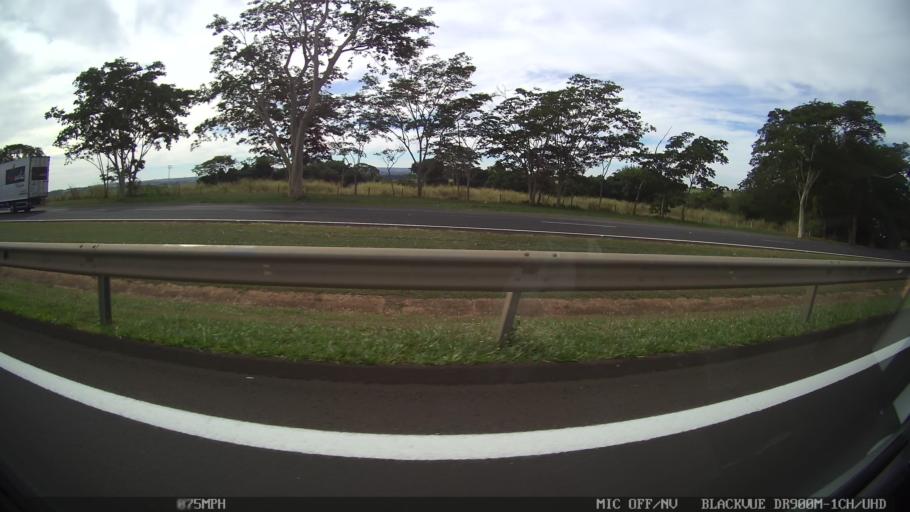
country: BR
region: Sao Paulo
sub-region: Taquaritinga
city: Taquaritinga
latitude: -21.4612
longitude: -48.6194
